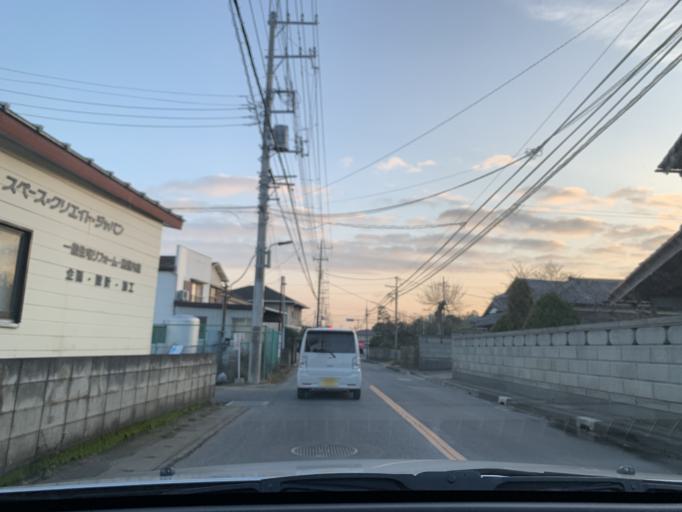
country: JP
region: Chiba
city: Matsudo
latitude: 35.7607
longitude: 139.9188
